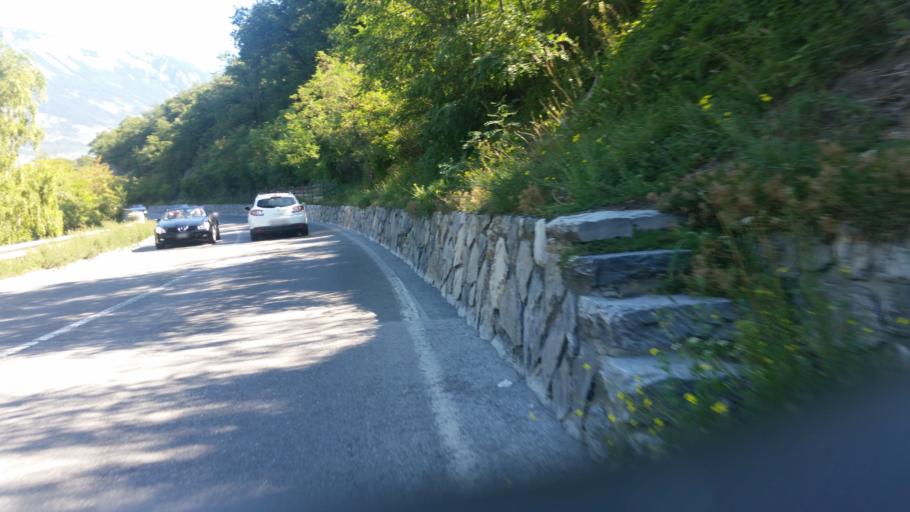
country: CH
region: Valais
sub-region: Sierre District
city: Chippis
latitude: 46.2870
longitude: 7.5430
